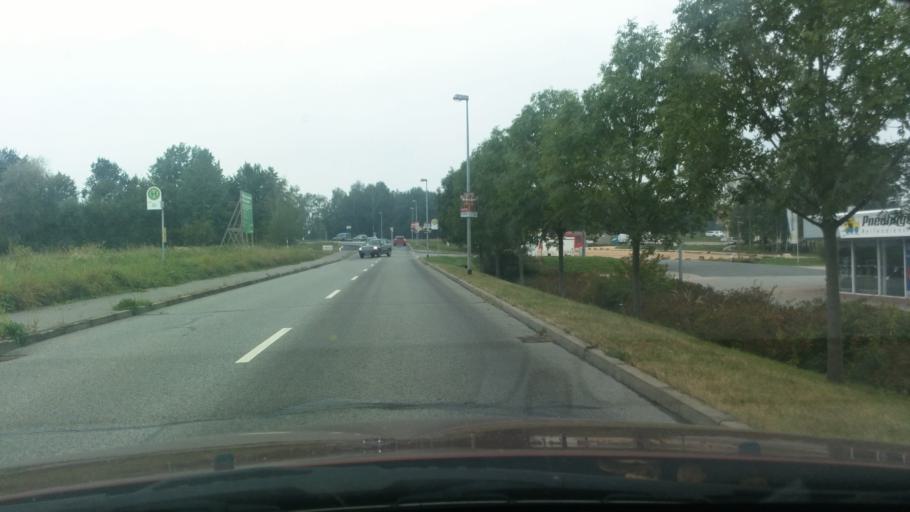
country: DE
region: Saxony
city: Goerlitz
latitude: 51.1820
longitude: 14.9640
